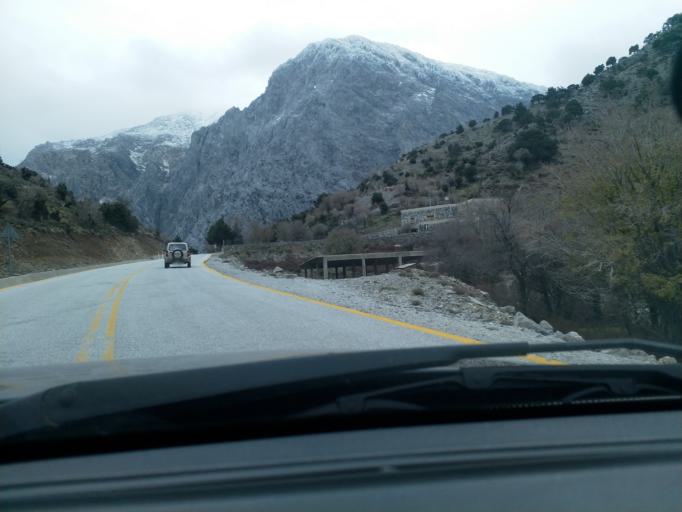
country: GR
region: Crete
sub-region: Nomos Chanias
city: Perivolia
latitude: 35.3106
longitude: 23.9171
